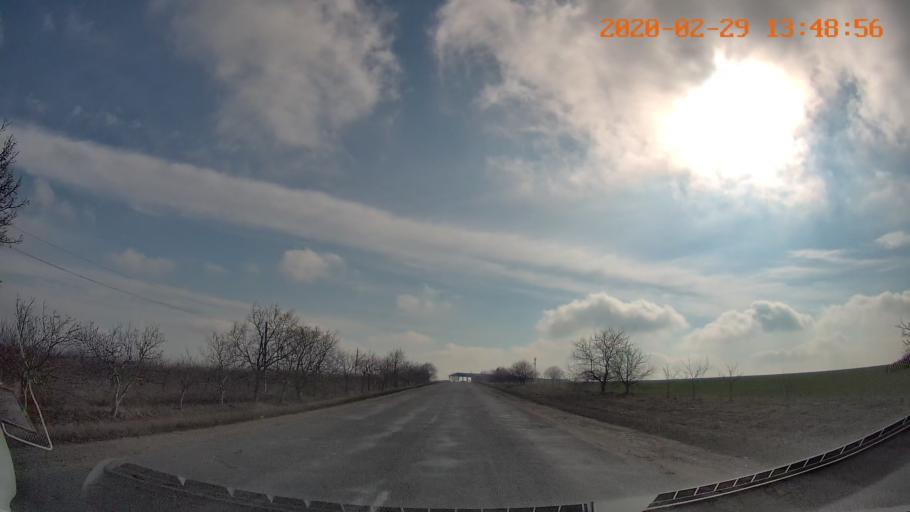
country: MD
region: Floresti
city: Leninskiy
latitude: 47.8485
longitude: 28.4878
